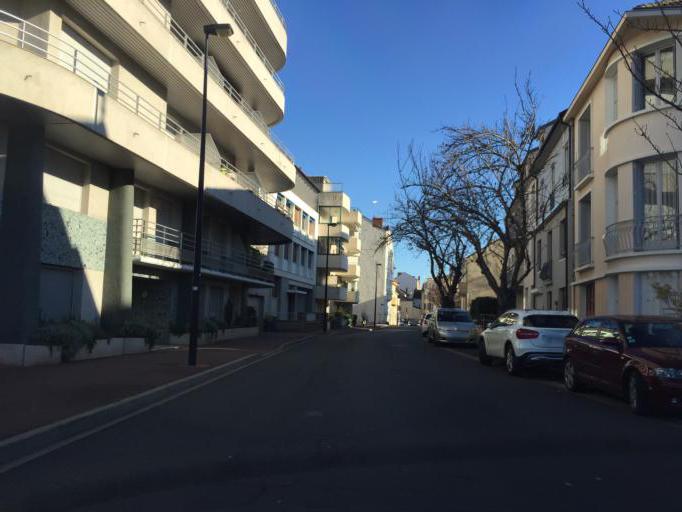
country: FR
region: Auvergne
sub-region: Departement de l'Allier
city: Vichy
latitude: 46.1297
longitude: 3.4165
